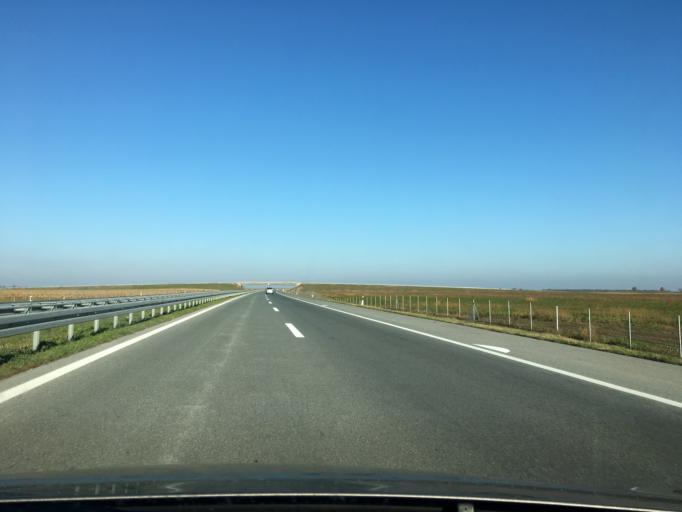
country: RS
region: Autonomna Pokrajina Vojvodina
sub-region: Severnobacki Okrug
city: Mali Igos
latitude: 45.7272
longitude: 19.7066
